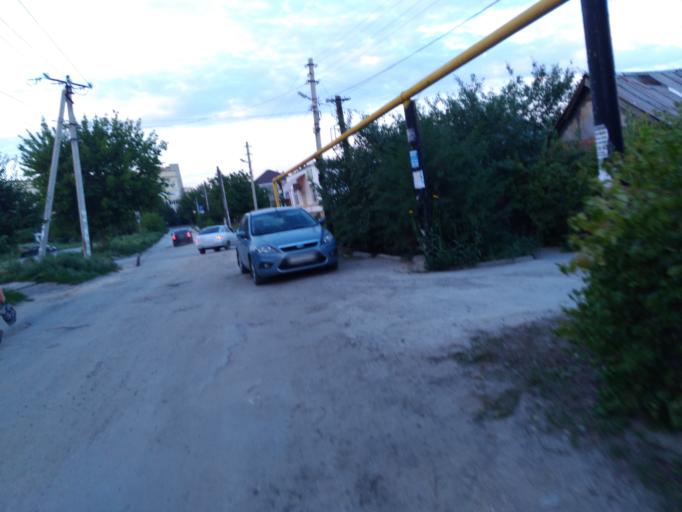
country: RU
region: Volgograd
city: Volgograd
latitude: 48.6710
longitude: 44.4509
